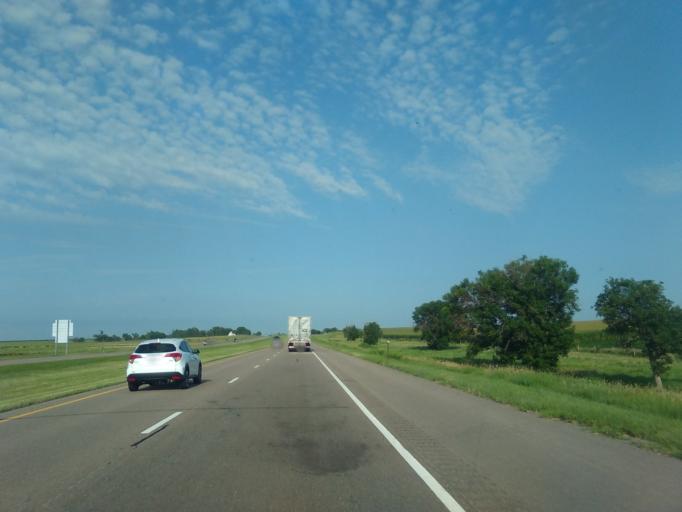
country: US
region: Nebraska
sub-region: York County
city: York
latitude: 40.8212
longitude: -97.6756
